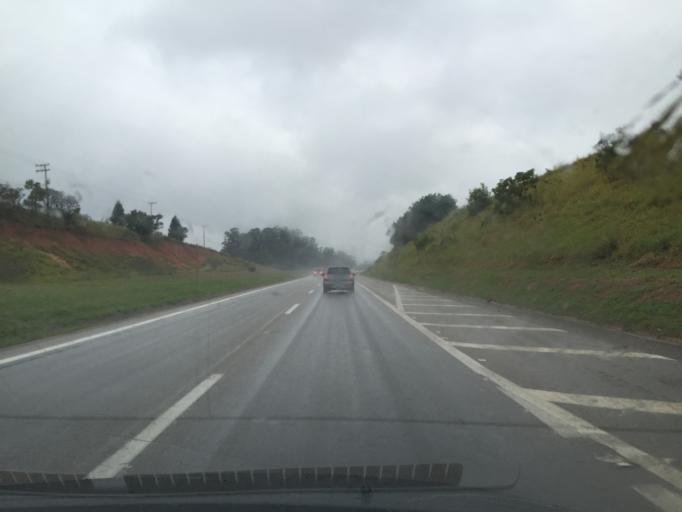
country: BR
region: Sao Paulo
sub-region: Itu
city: Itu
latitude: -23.3789
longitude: -47.3275
